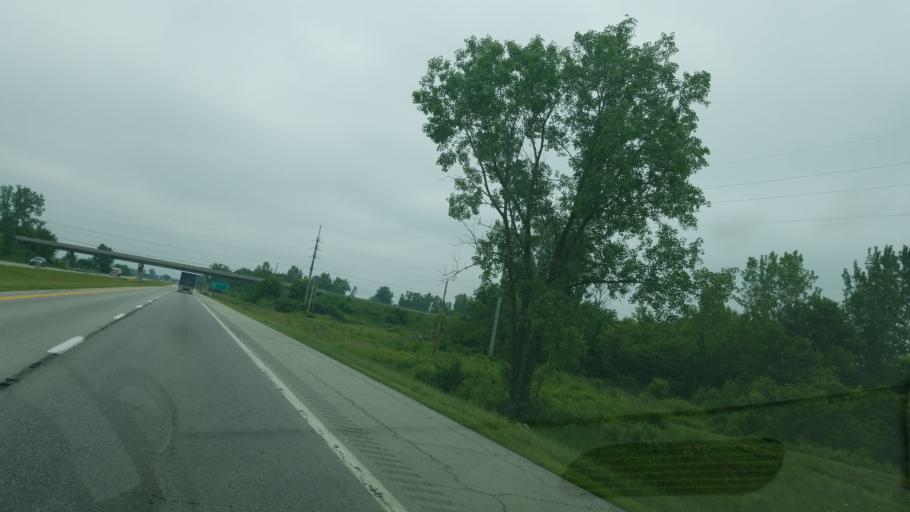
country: US
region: Ohio
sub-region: Marion County
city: Marion
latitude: 40.6279
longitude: -83.0965
